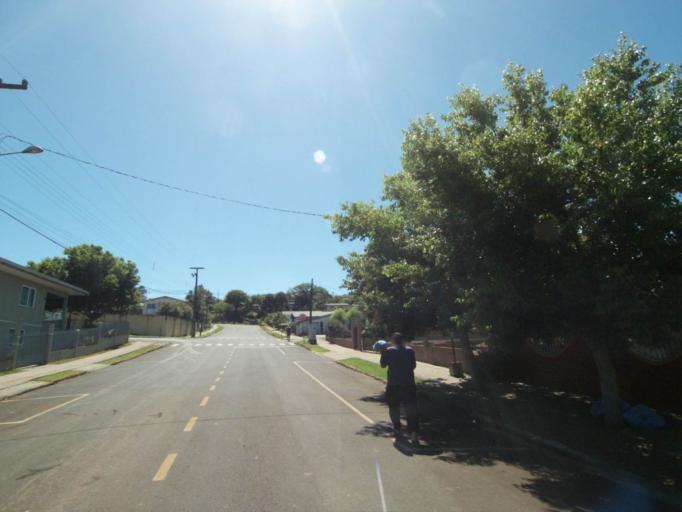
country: BR
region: Parana
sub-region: Pato Branco
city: Pato Branco
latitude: -26.2669
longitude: -52.7760
